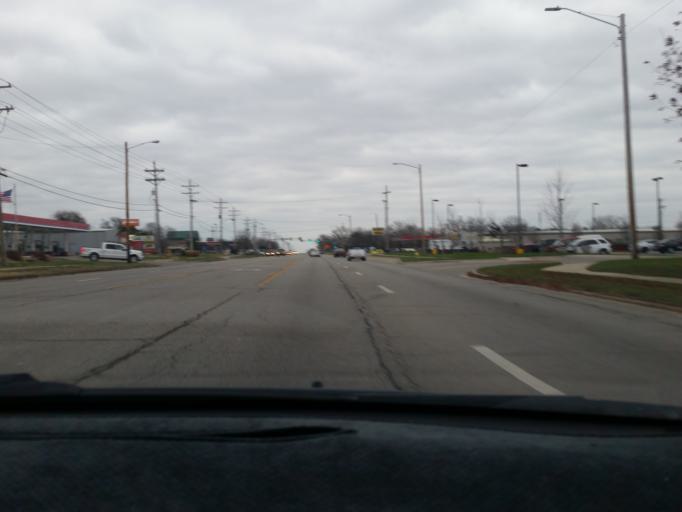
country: US
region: Kansas
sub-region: Douglas County
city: Lawrence
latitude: 38.9427
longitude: -95.2176
